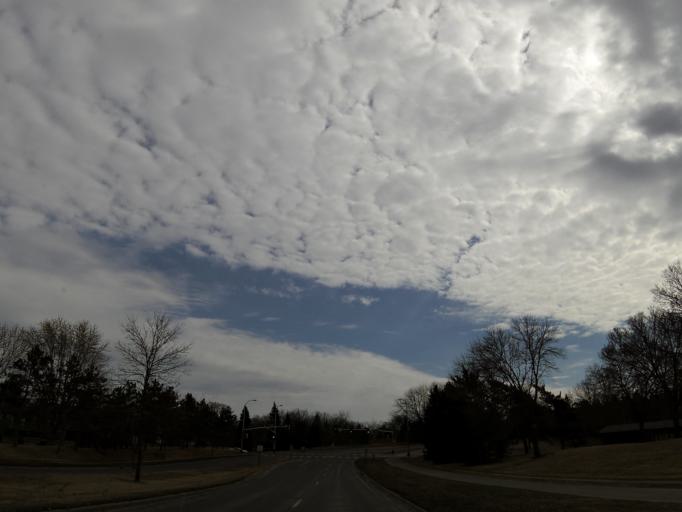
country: US
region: Minnesota
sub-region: Scott County
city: Savage
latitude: 44.8179
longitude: -93.3858
